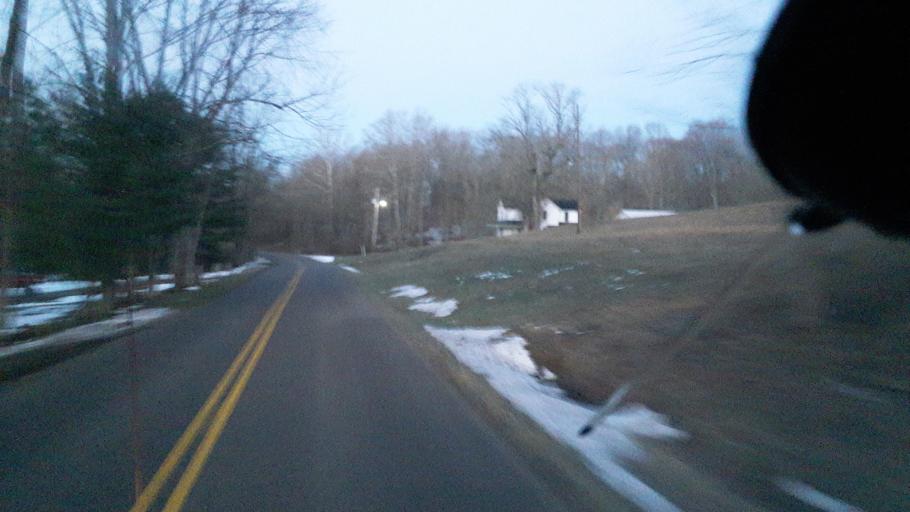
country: US
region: Ohio
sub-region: Perry County
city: New Lexington
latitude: 39.7050
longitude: -82.2540
